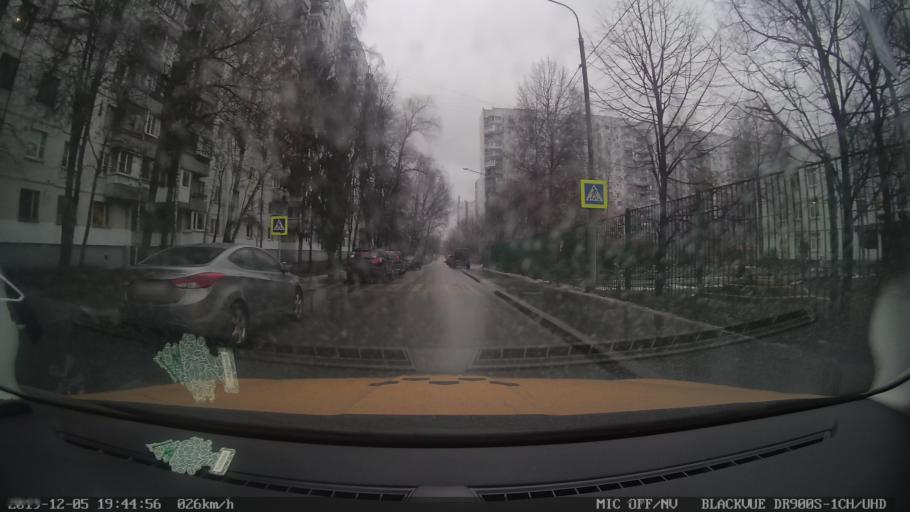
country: RU
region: Moscow
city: Lianozovo
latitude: 55.9015
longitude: 37.5771
